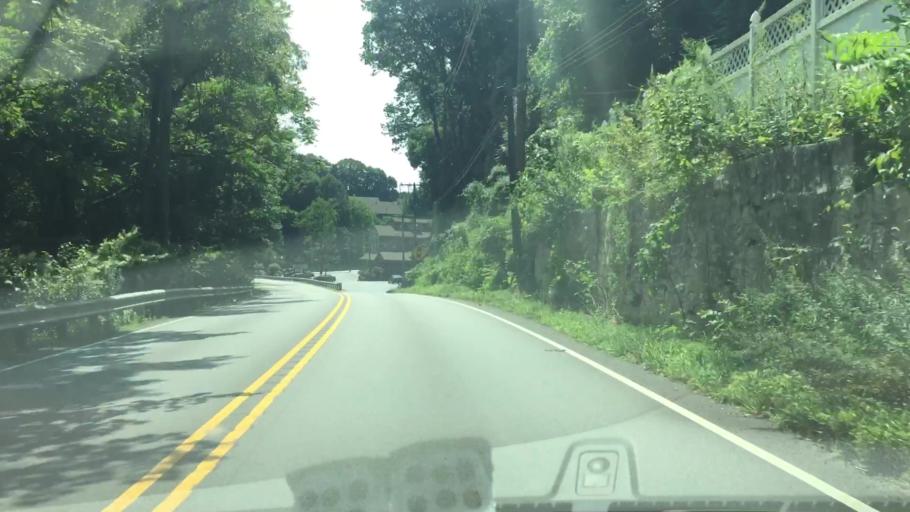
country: US
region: Pennsylvania
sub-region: Delaware County
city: Village Green-Green Ridge
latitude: 39.8857
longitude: -75.4311
